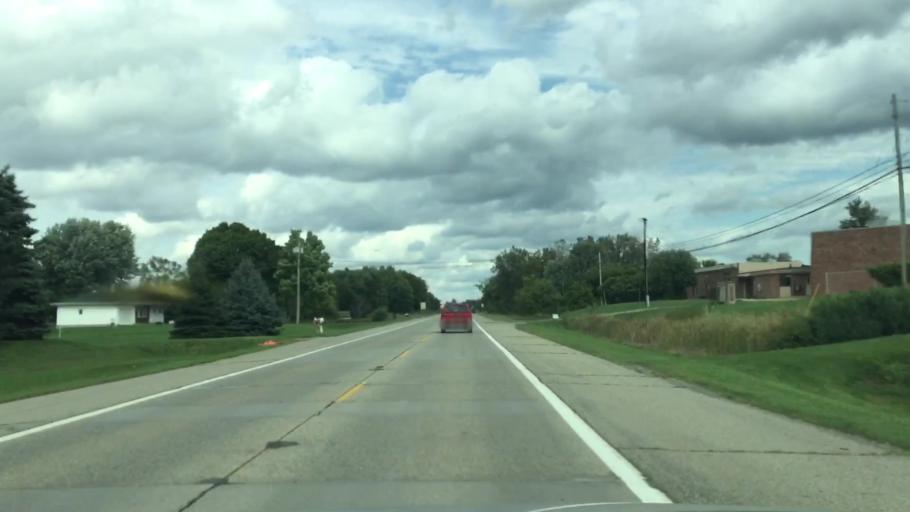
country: US
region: Michigan
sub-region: Shiawassee County
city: Owosso
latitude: 42.9638
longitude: -84.1993
